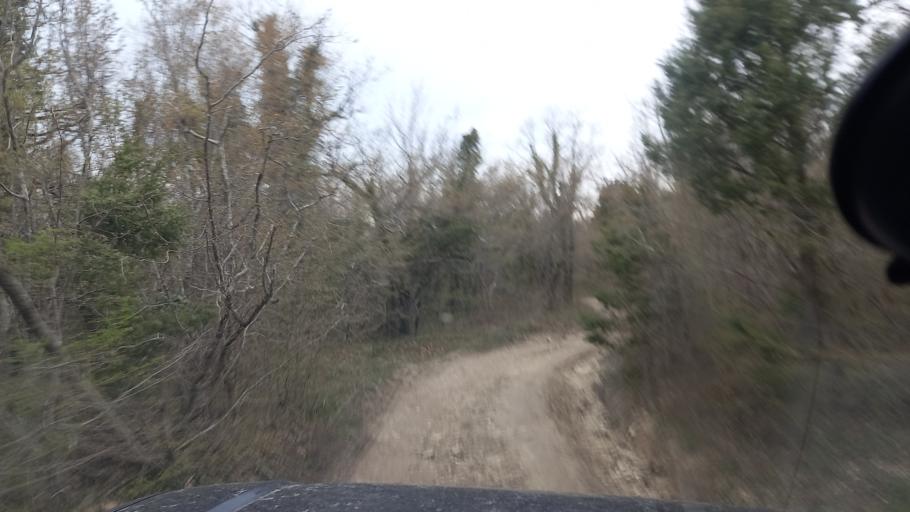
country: RU
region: Krasnodarskiy
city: Dzhubga
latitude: 44.3163
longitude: 38.6794
